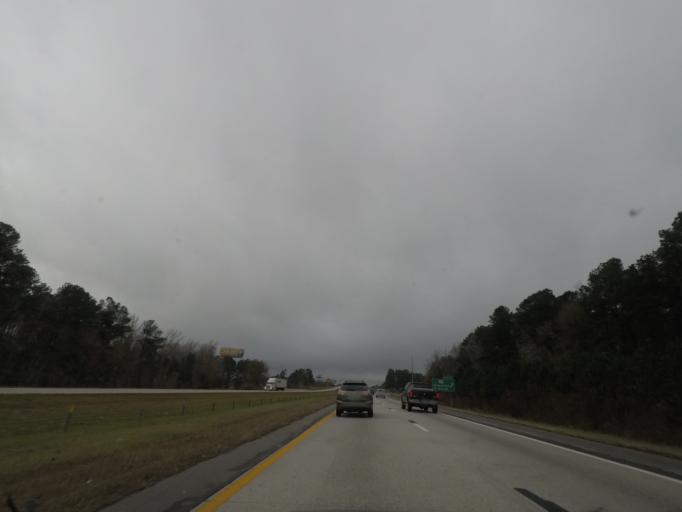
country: US
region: South Carolina
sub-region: Dorchester County
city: Saint George
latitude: 33.2000
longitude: -80.6033
